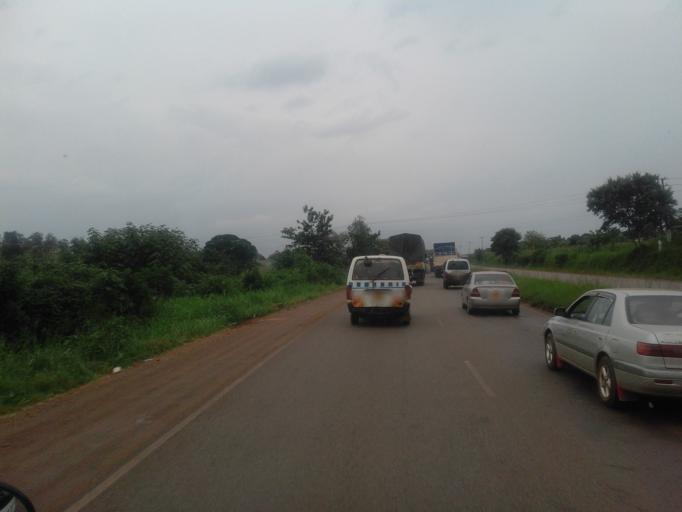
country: UG
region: Eastern Region
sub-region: Jinja District
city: Jinja
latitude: 0.4457
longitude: 33.2039
